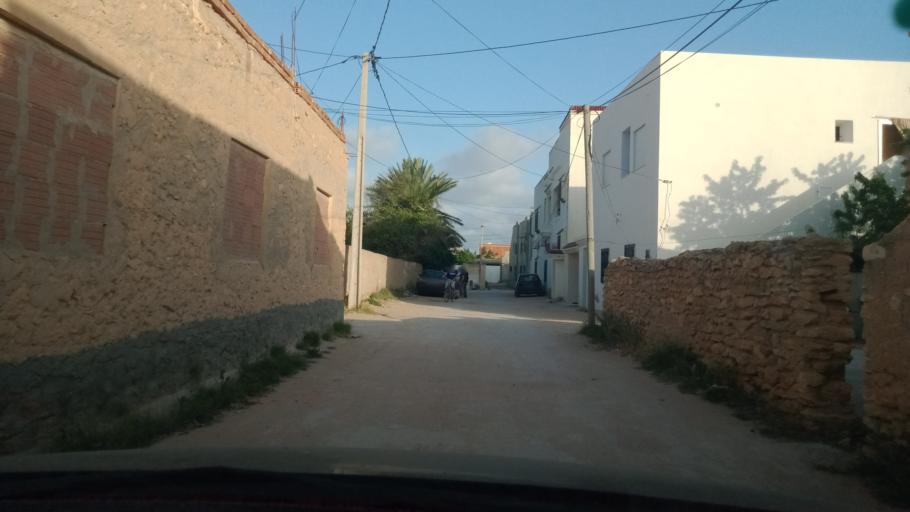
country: TN
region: Safaqis
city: Al Qarmadah
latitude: 34.8170
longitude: 10.7492
